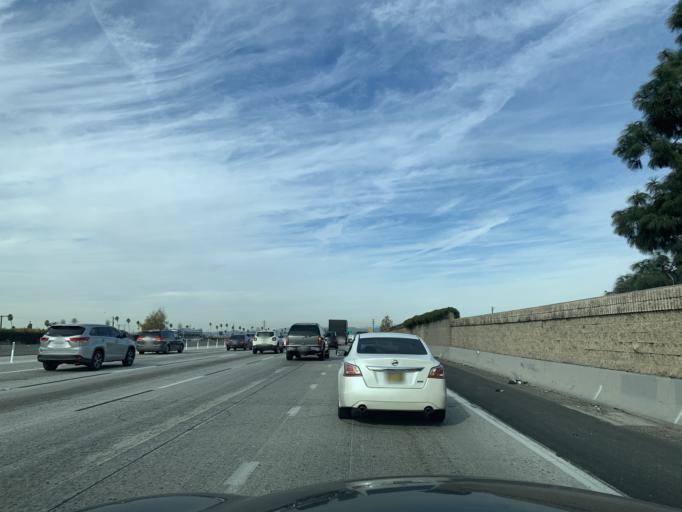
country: US
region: California
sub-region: Los Angeles County
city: Westmont
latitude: 33.9518
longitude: -118.2797
